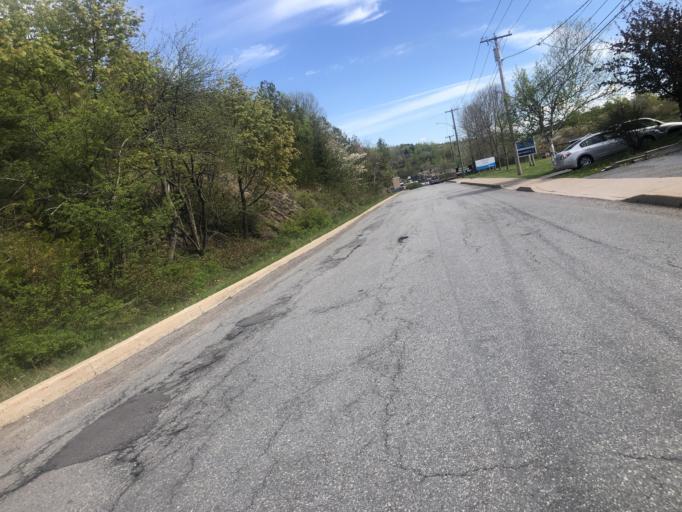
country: CA
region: New Brunswick
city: Saint John
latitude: 45.2855
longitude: -66.0825
